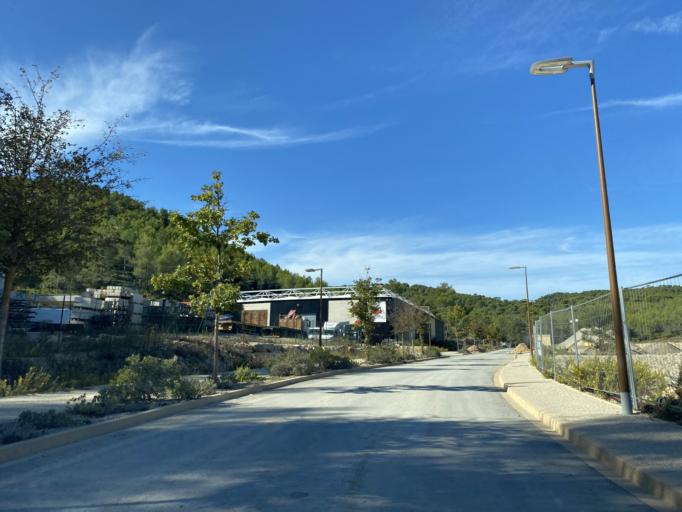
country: FR
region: Provence-Alpes-Cote d'Azur
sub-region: Departement des Bouches-du-Rhone
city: Ceyreste
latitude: 43.2120
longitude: 5.6011
